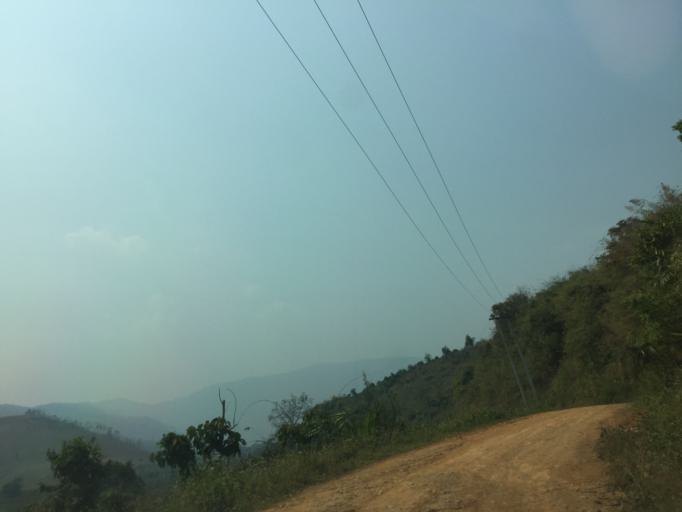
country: TH
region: Phayao
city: Phu Sang
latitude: 19.5812
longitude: 100.5285
